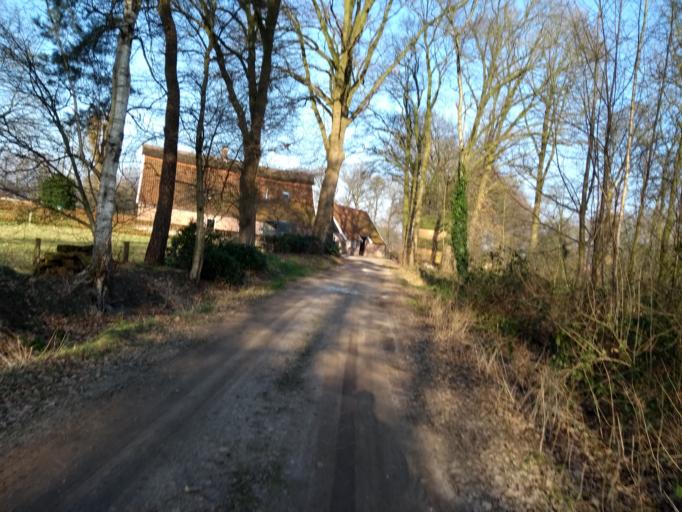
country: NL
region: Overijssel
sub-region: Gemeente Tubbergen
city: Tubbergen
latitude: 52.3910
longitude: 6.7325
